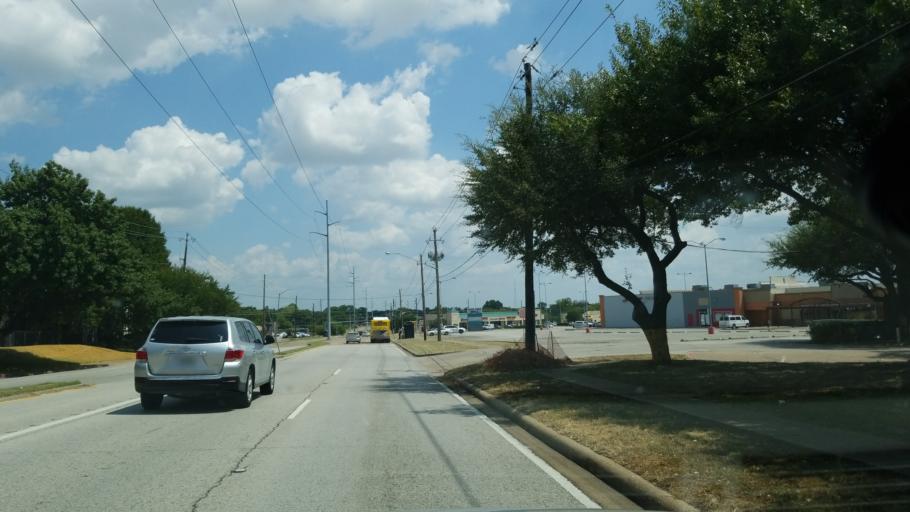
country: US
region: Texas
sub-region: Dallas County
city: Richardson
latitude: 32.9244
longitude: -96.7215
